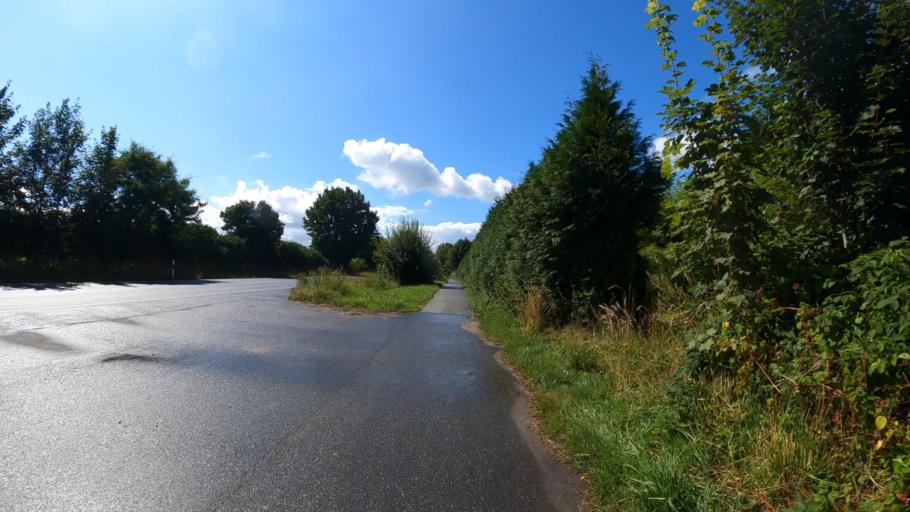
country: DE
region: Schleswig-Holstein
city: Fuhlendorf
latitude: 53.9408
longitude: 9.8950
